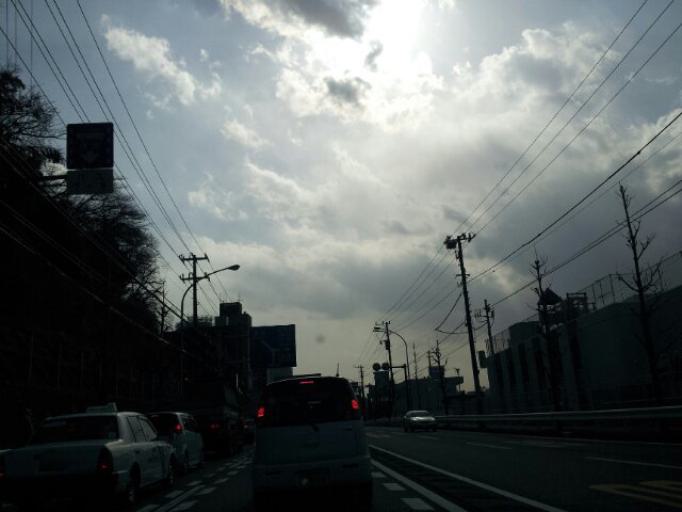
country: JP
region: Kanagawa
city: Yokohama
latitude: 35.4476
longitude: 139.6012
